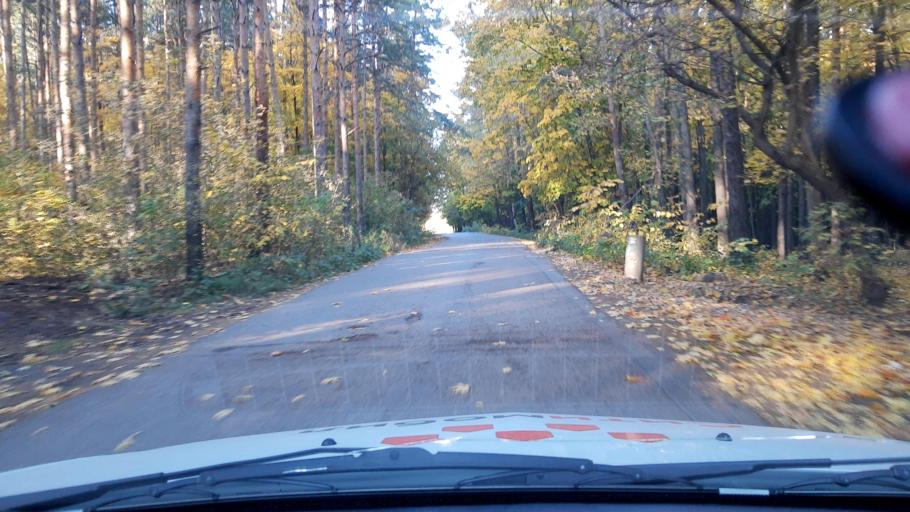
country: RU
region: Bashkortostan
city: Ufa
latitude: 54.7049
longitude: 56.0114
